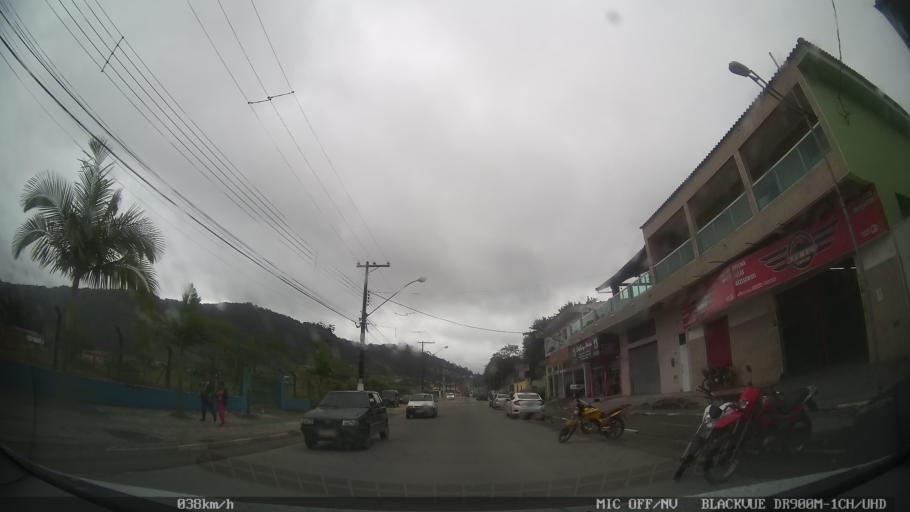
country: BR
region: Sao Paulo
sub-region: Juquia
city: Juquia
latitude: -24.3178
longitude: -47.6343
